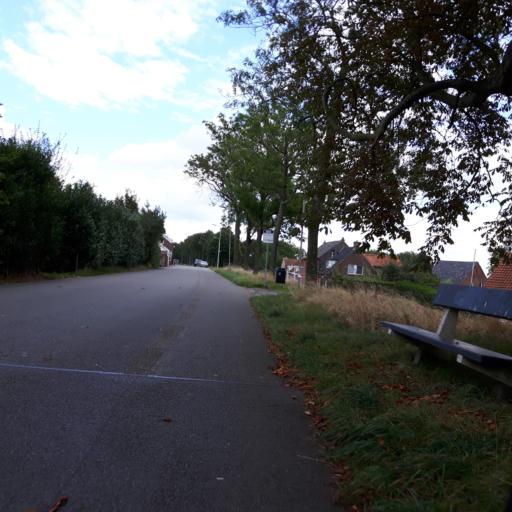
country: NL
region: Zeeland
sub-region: Gemeente Goes
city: Goes
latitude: 51.4935
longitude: 3.8209
